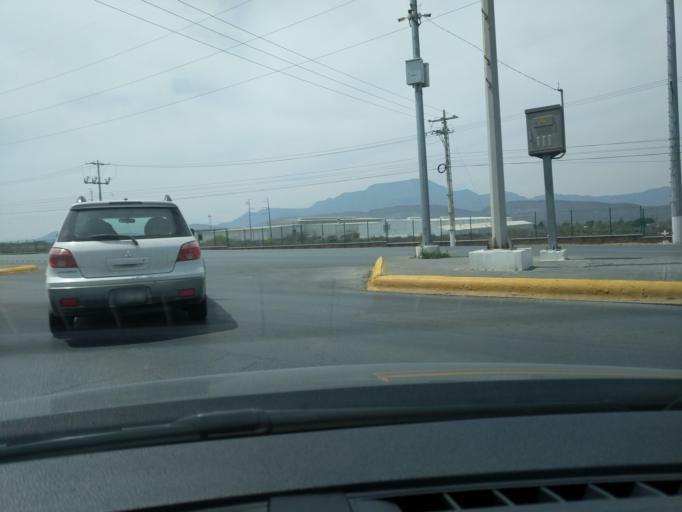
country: MX
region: Coahuila
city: Saltillo
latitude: 25.3577
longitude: -101.0200
